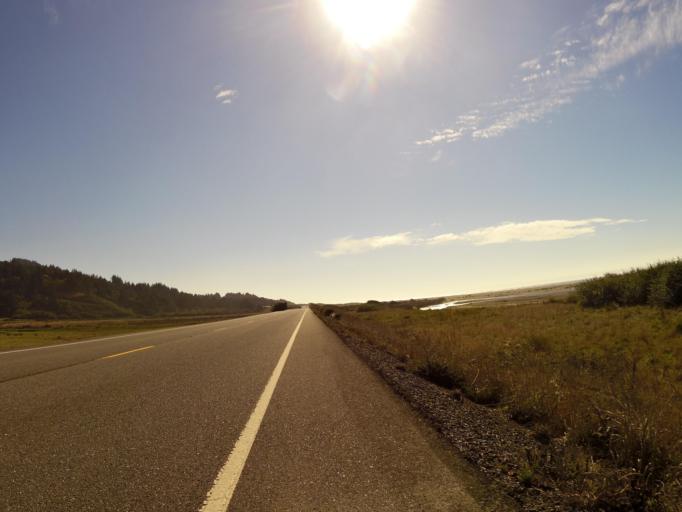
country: US
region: Oregon
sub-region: Curry County
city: Gold Beach
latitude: 42.5600
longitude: -124.3873
